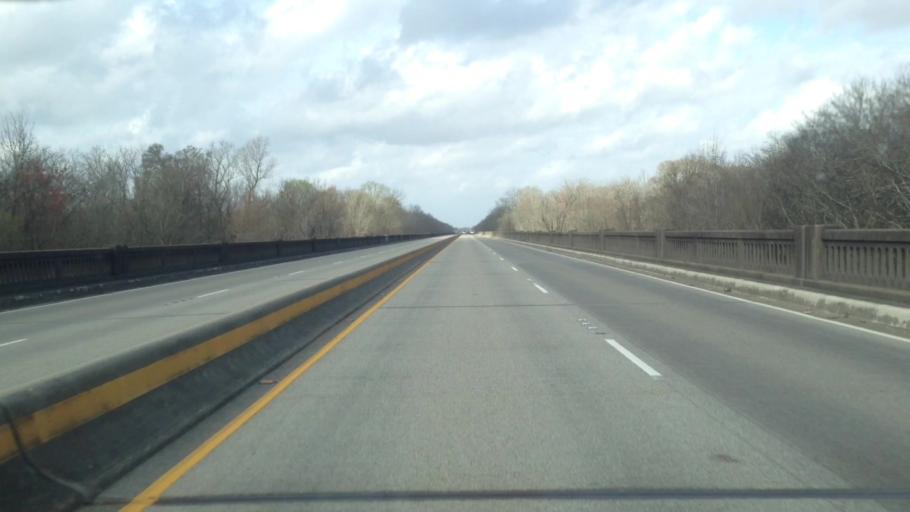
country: US
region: Louisiana
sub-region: Saint Landry Parish
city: Krotz Springs
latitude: 30.5542
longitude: -91.6952
